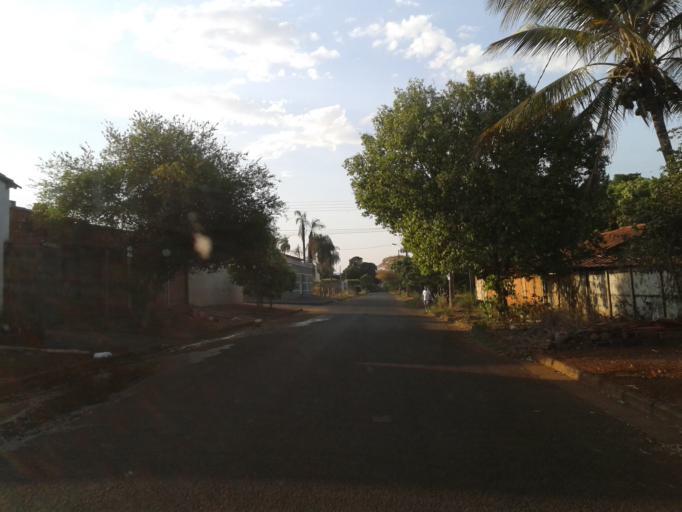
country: BR
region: Minas Gerais
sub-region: Ituiutaba
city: Ituiutaba
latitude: -18.9841
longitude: -49.4451
